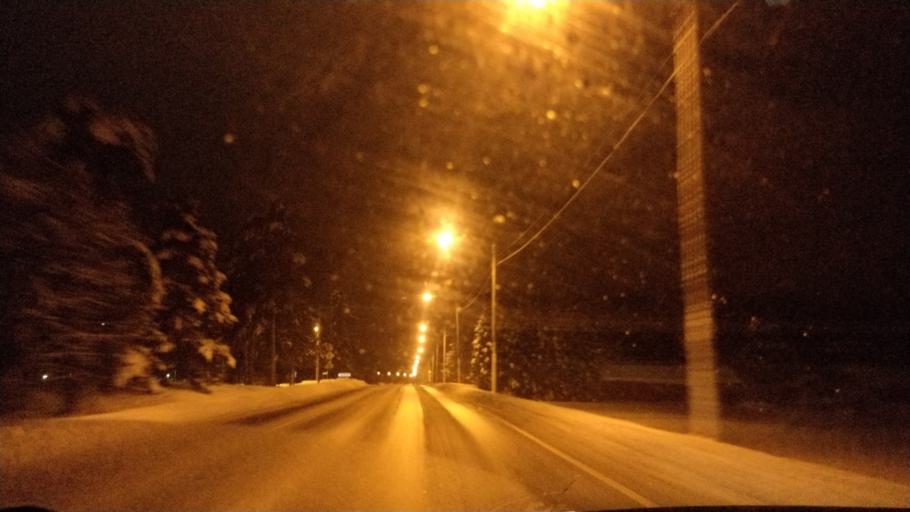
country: FI
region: Lapland
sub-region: Rovaniemi
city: Rovaniemi
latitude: 66.2727
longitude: 25.3298
